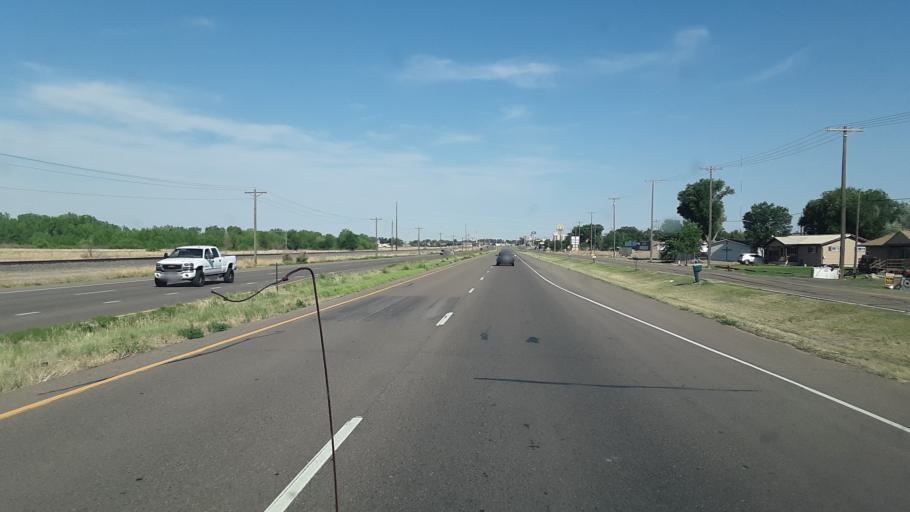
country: US
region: Colorado
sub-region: Otero County
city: La Junta
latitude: 37.9944
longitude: -103.5768
